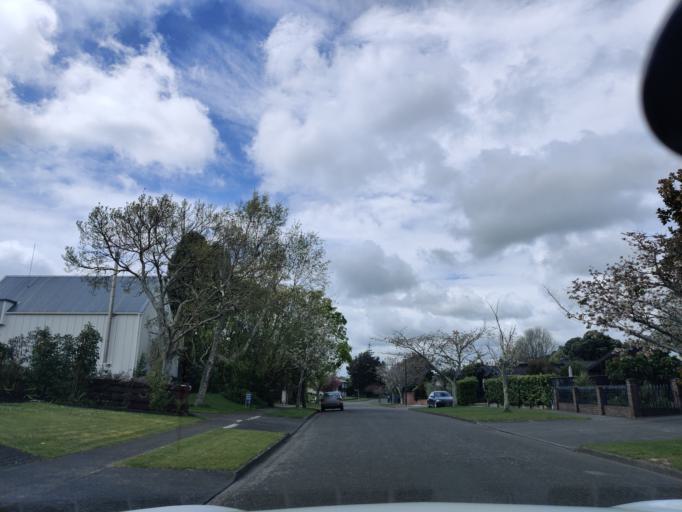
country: NZ
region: Manawatu-Wanganui
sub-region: Palmerston North City
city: Palmerston North
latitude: -40.3812
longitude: 175.5921
